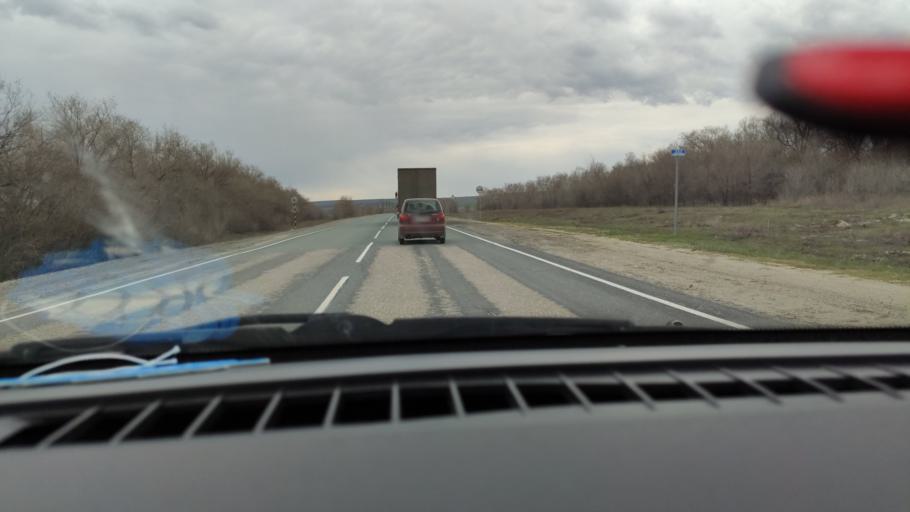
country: RU
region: Saratov
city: Sinodskoye
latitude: 51.9348
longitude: 46.5890
